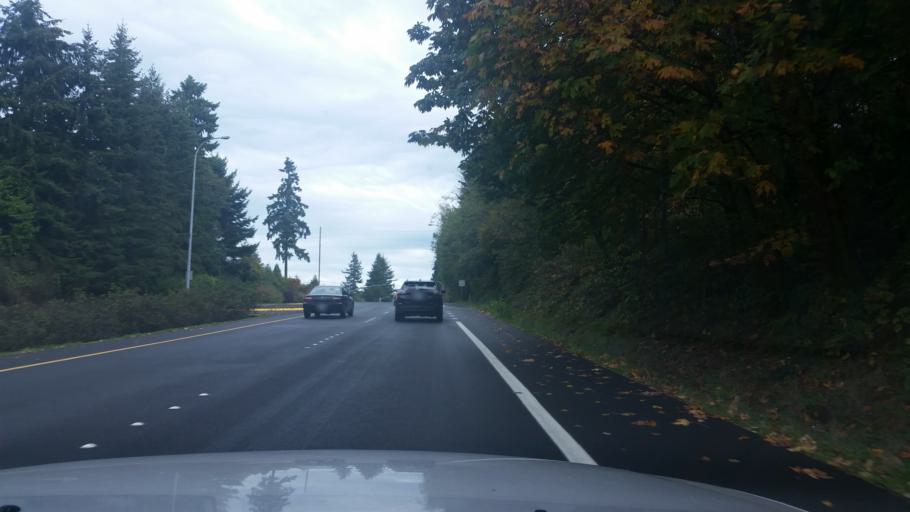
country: US
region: Washington
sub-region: King County
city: Eastgate
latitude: 47.6026
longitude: -122.1563
